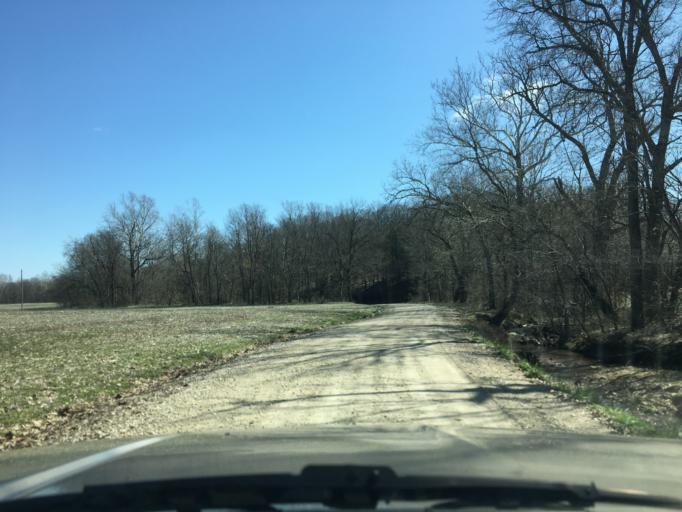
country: US
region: Missouri
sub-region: Franklin County
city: New Haven
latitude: 38.5533
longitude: -91.3262
